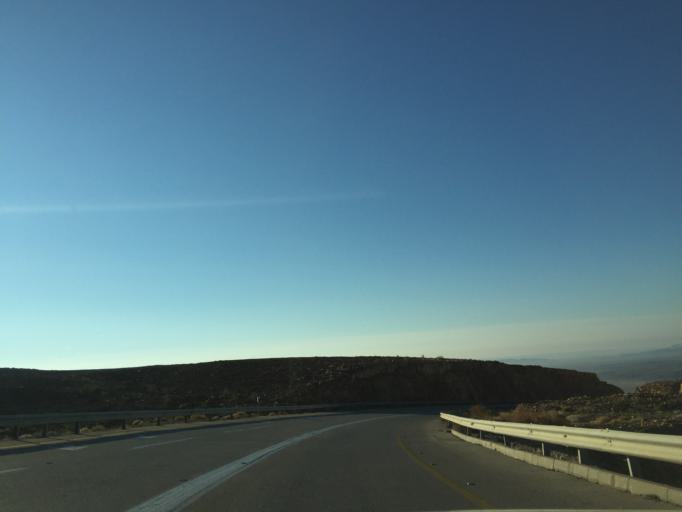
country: IL
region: Southern District
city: Mitzpe Ramon
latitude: 30.5056
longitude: 34.9455
